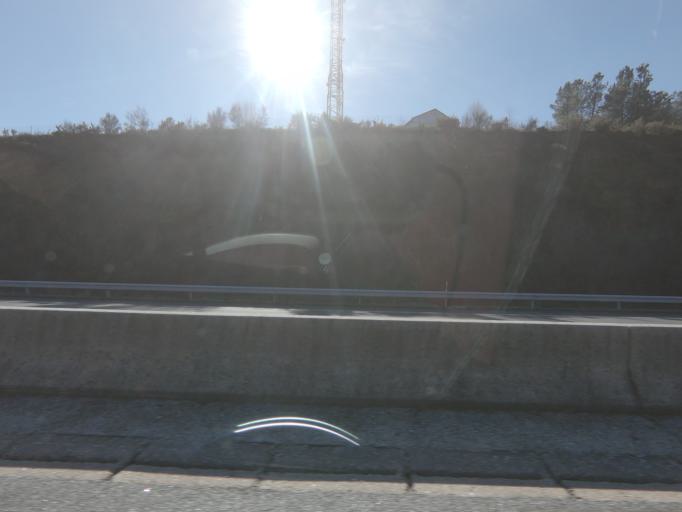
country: ES
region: Galicia
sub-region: Provincia de Pontevedra
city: Dozon
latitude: 42.5613
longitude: -8.0319
